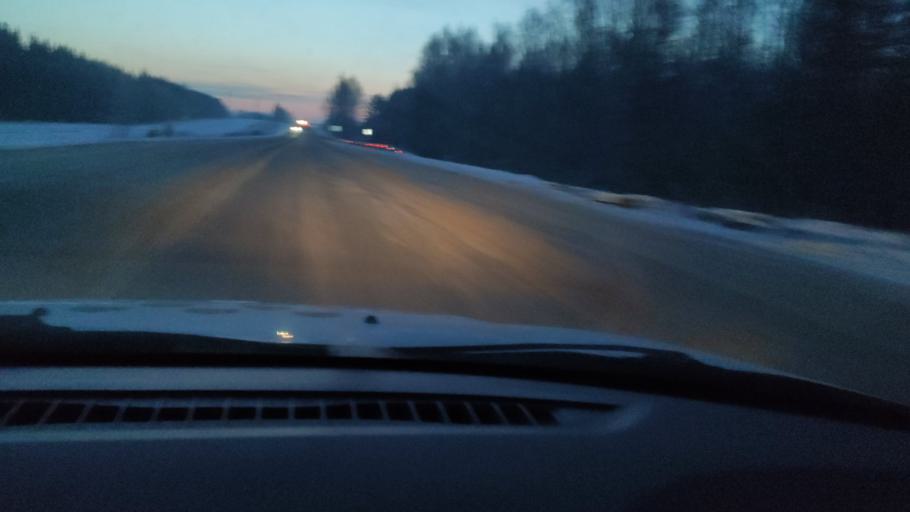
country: RU
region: Perm
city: Kungur
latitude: 57.4092
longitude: 56.9042
